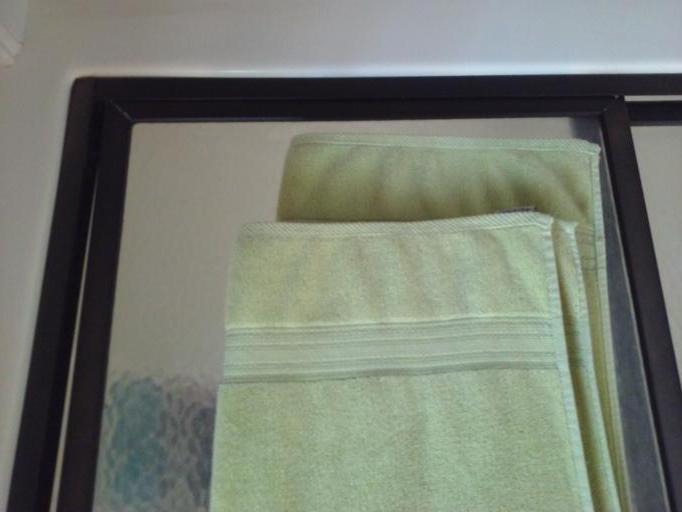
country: US
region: North Carolina
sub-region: Wake County
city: Fuquay-Varina
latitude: 35.5455
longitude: -78.8725
